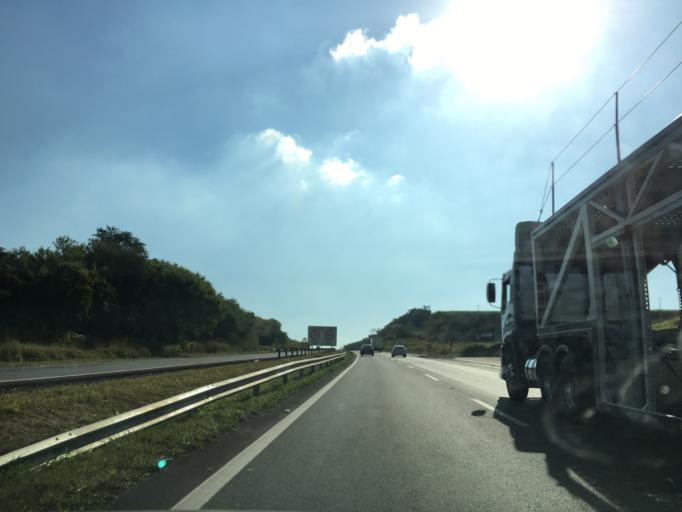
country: BR
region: Sao Paulo
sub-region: Piracicaba
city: Piracicaba
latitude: -22.7295
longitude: -47.5448
